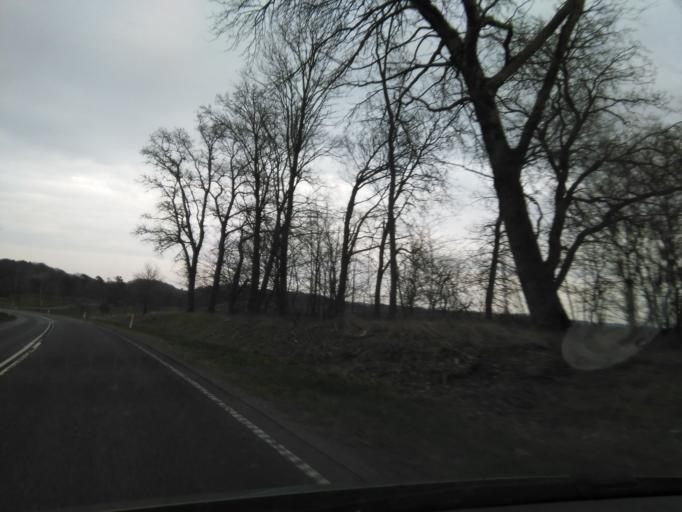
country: DK
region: North Denmark
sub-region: Mariagerfjord Kommune
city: Mariager
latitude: 56.6884
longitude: 9.9908
